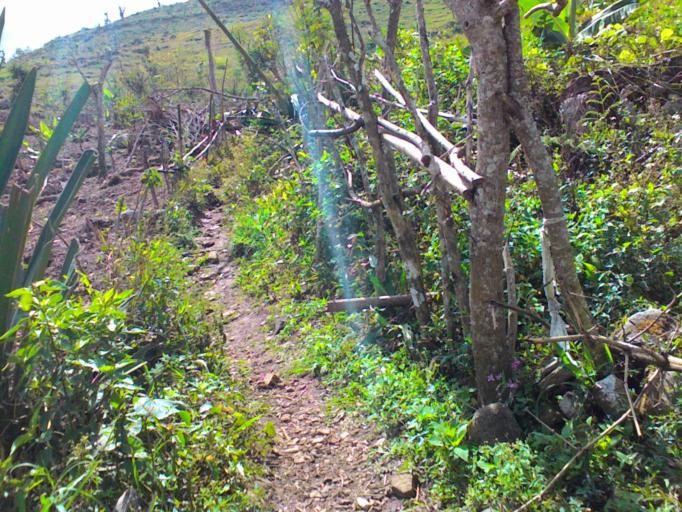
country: HT
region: Sud
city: Les Anglais
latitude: 18.4514
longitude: -74.1051
